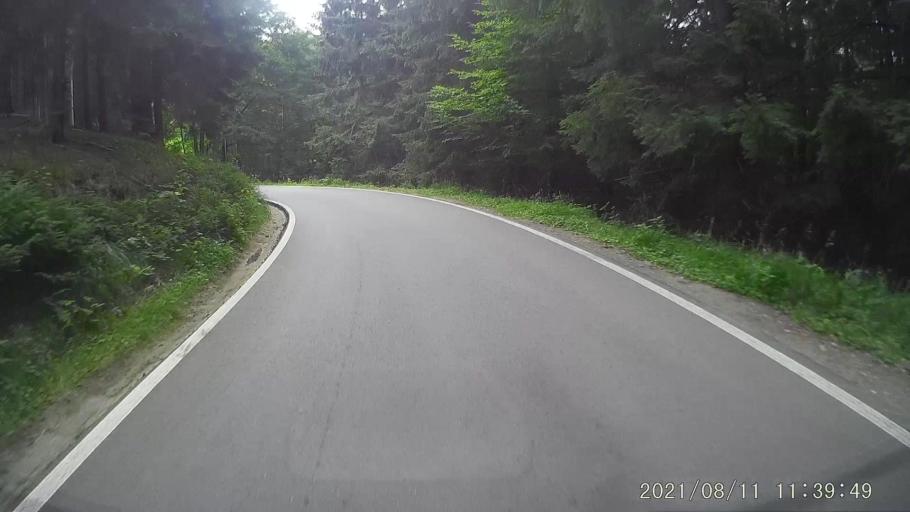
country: PL
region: Lower Silesian Voivodeship
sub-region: Powiat klodzki
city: Stronie Slaskie
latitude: 50.2554
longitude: 16.8286
